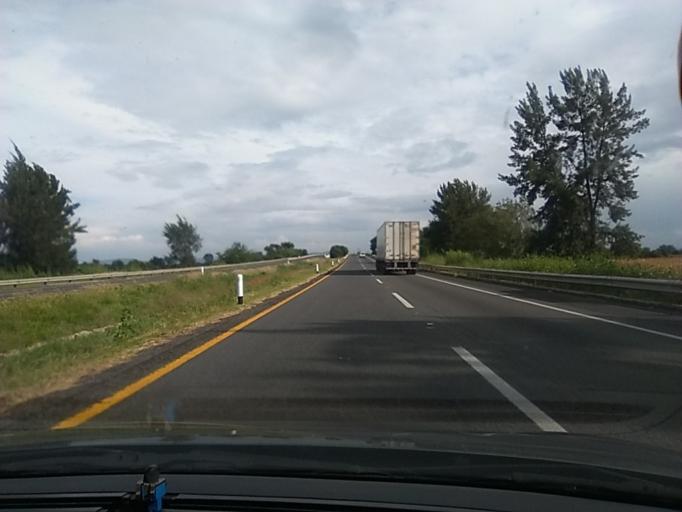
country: MX
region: Michoacan
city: Vistahermosa de Negrete
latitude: 20.3104
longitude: -102.4940
